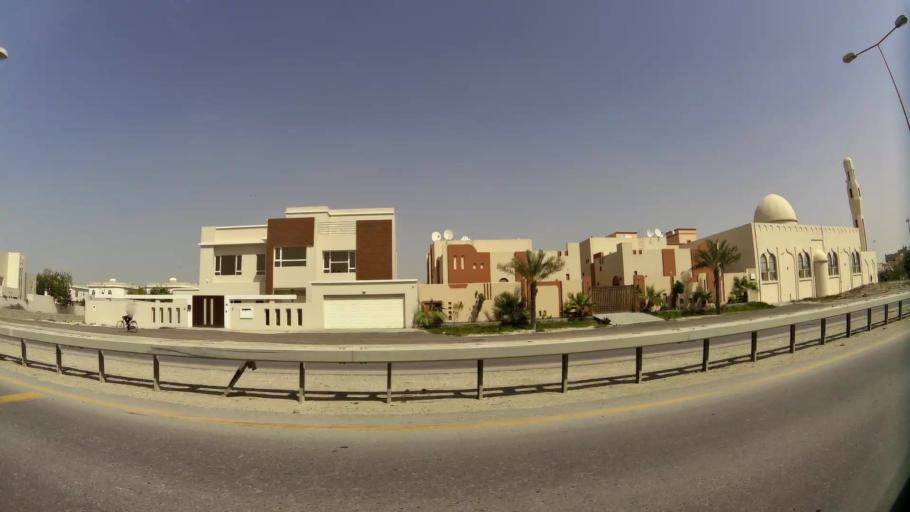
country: BH
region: Manama
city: Jidd Hafs
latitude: 26.1977
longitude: 50.4609
